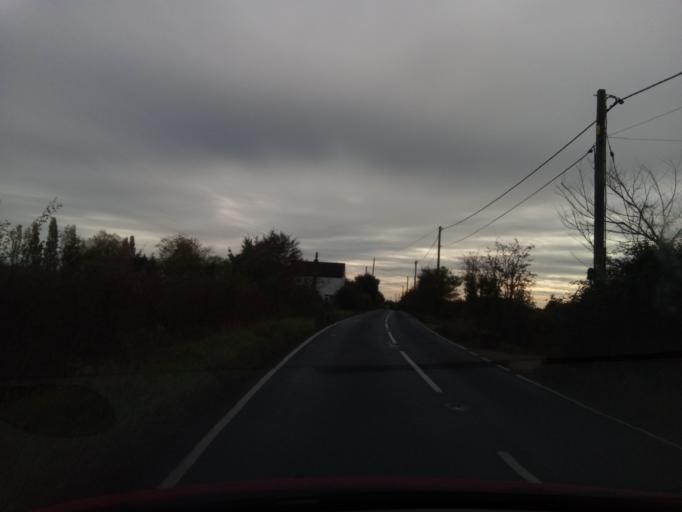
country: GB
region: England
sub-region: Essex
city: West Mersea
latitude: 51.8066
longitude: 0.9053
